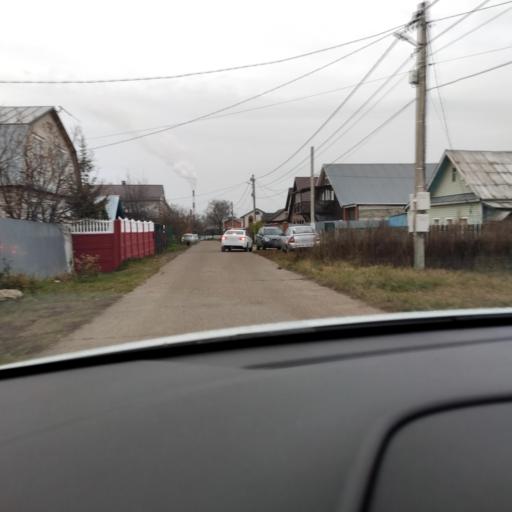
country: RU
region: Tatarstan
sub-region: Gorod Kazan'
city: Kazan
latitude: 55.8638
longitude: 49.0612
